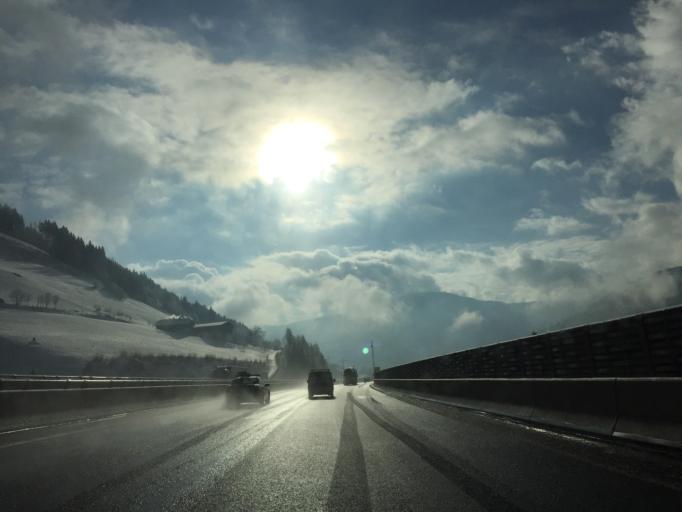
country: AT
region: Salzburg
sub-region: Politischer Bezirk Sankt Johann im Pongau
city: Huttau
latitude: 47.4280
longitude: 13.2953
